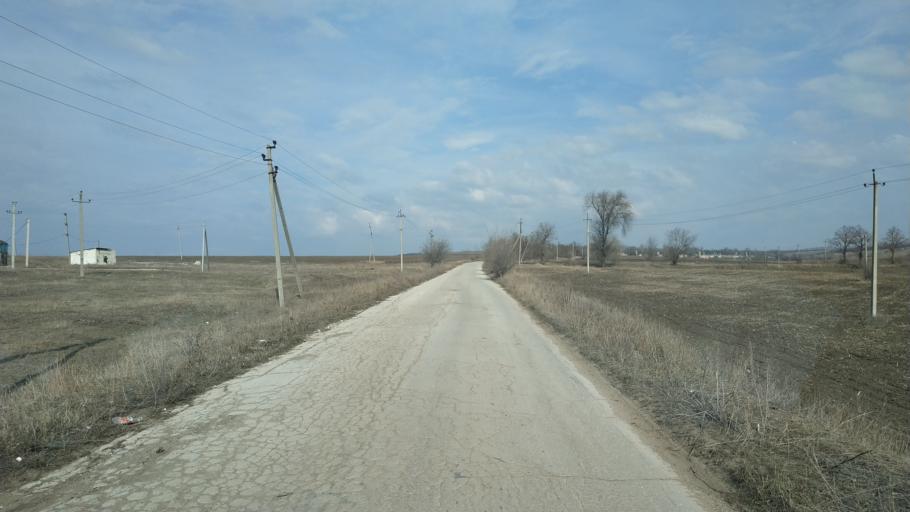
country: MD
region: Anenii Noi
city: Anenii Noi
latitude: 46.9329
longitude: 29.1071
